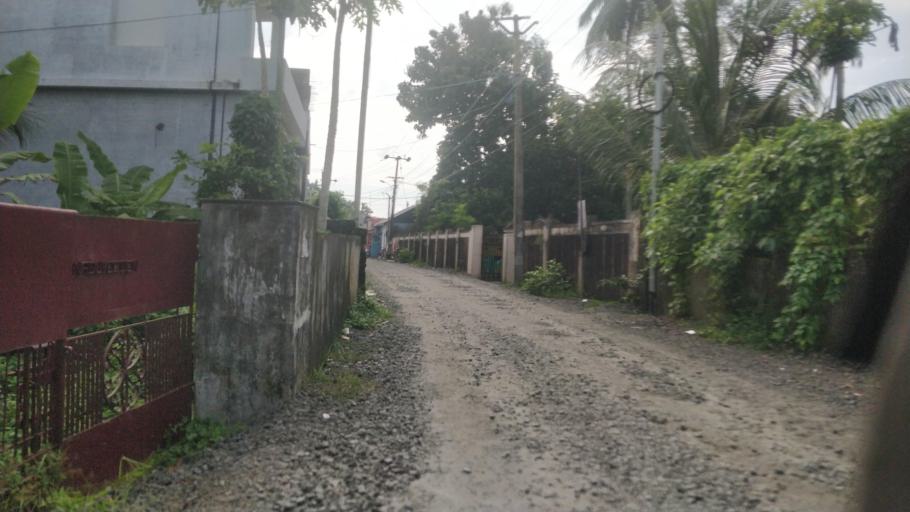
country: IN
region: Kerala
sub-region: Alappuzha
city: Vayalar
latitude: 9.6912
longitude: 76.3362
